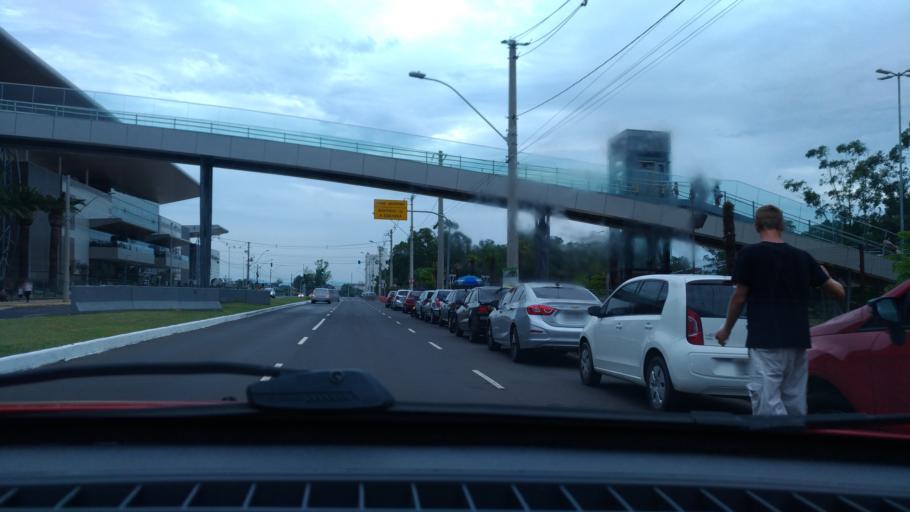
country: BR
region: Rio Grande do Sul
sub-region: Canoas
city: Canoas
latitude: -29.9137
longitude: -51.1657
